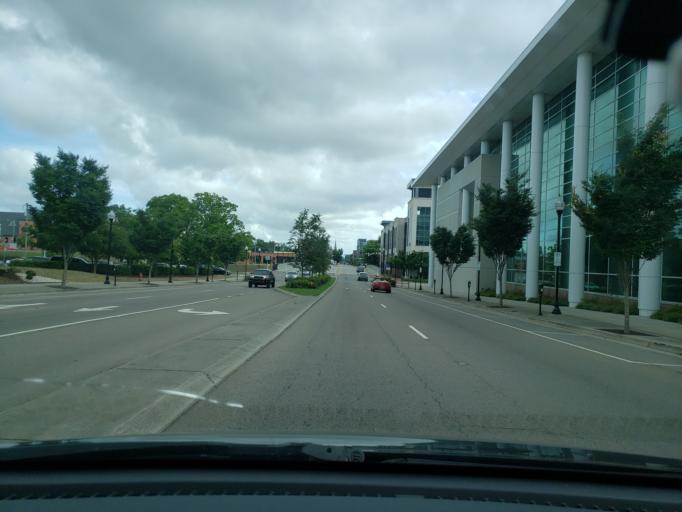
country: US
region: North Carolina
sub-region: New Hanover County
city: Wilmington
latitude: 34.2443
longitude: -77.9471
